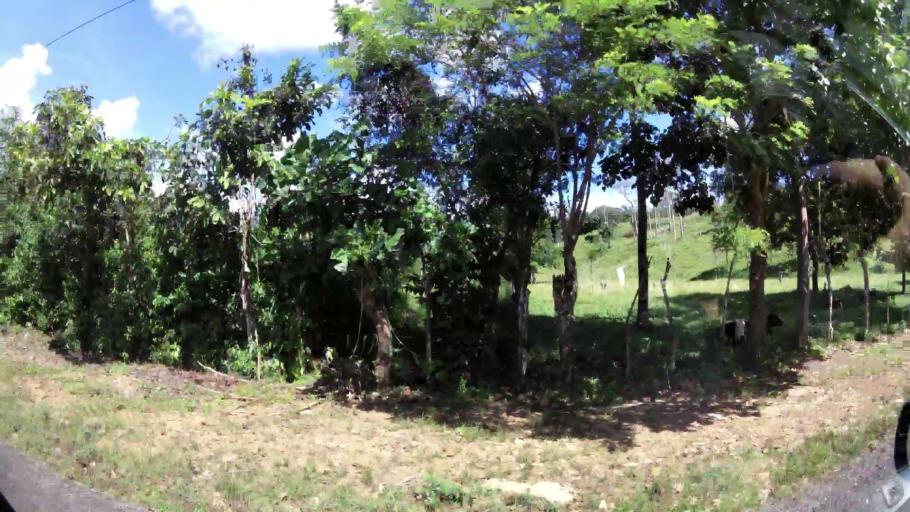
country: CR
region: San Jose
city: San Isidro
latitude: 9.3864
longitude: -83.6998
